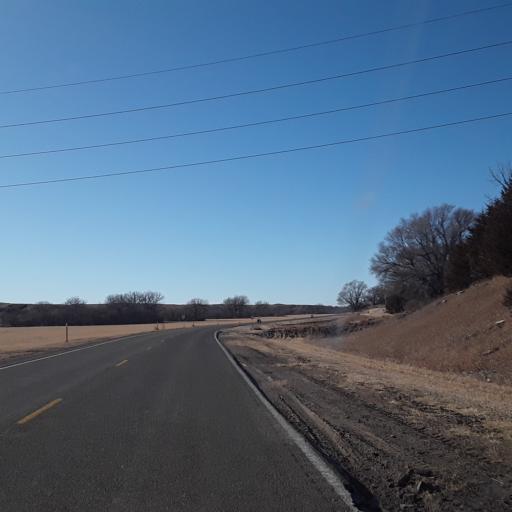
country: US
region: Nebraska
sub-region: Frontier County
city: Stockville
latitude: 40.6287
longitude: -100.5273
